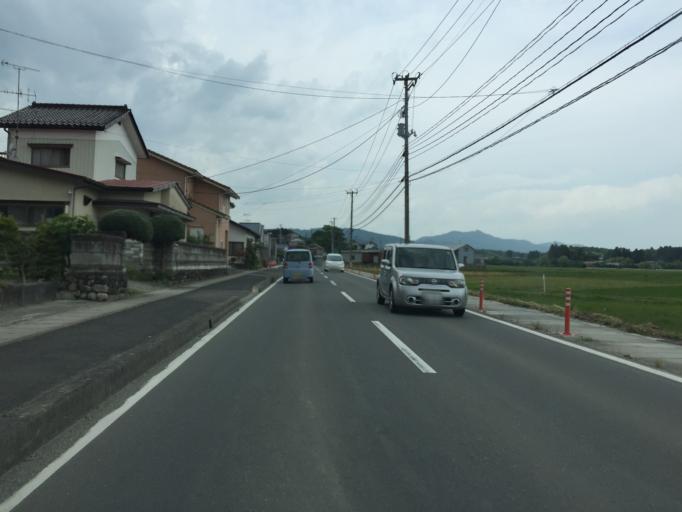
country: JP
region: Miyagi
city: Marumori
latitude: 37.8075
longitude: 140.9038
